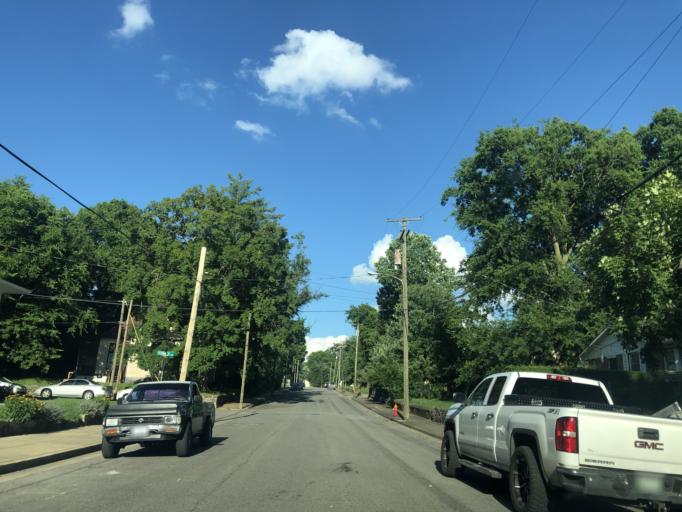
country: US
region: Tennessee
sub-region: Davidson County
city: Nashville
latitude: 36.1882
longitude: -86.7672
